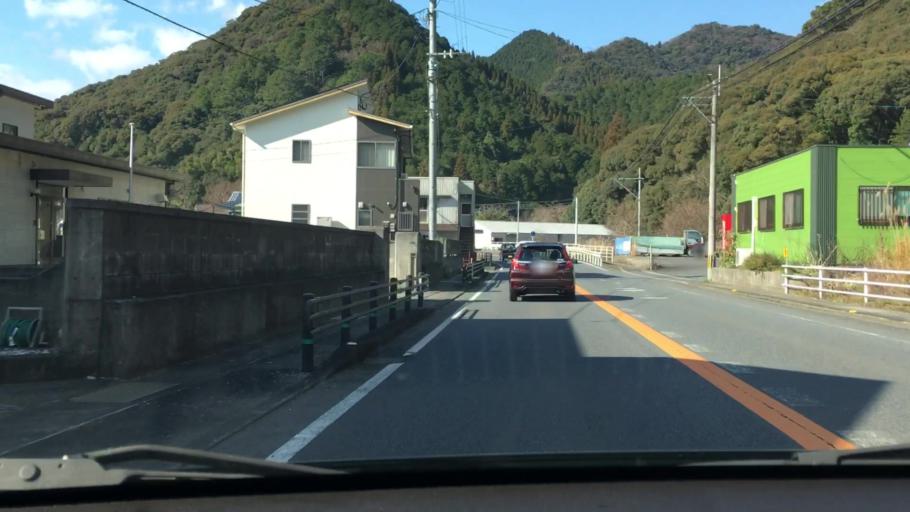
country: JP
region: Oita
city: Saiki
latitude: 32.9856
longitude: 131.8472
